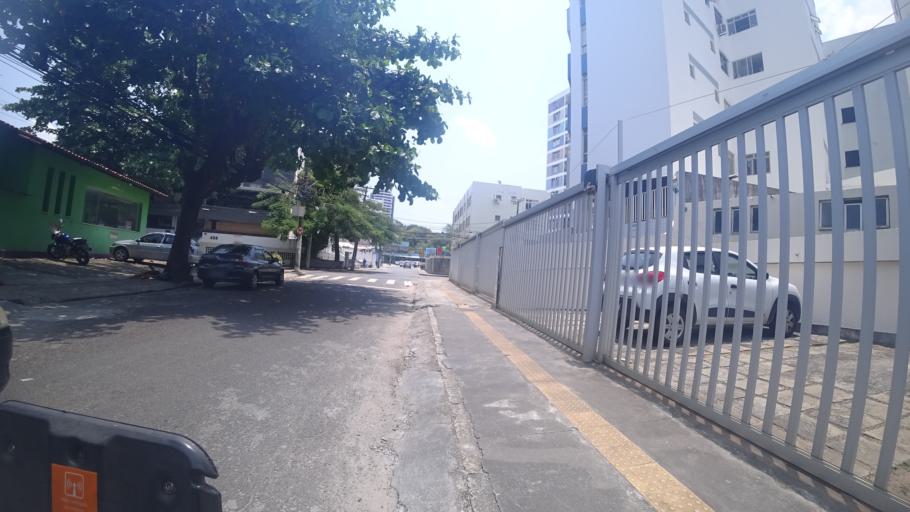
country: BR
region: Bahia
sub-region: Salvador
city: Salvador
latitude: -12.9925
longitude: -38.4537
